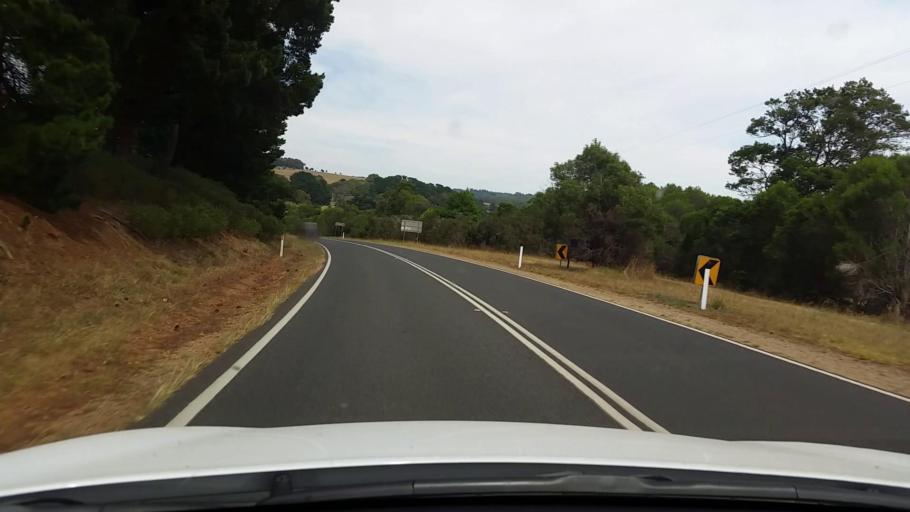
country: AU
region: Victoria
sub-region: Mornington Peninsula
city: Merricks
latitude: -38.4035
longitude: 145.0704
